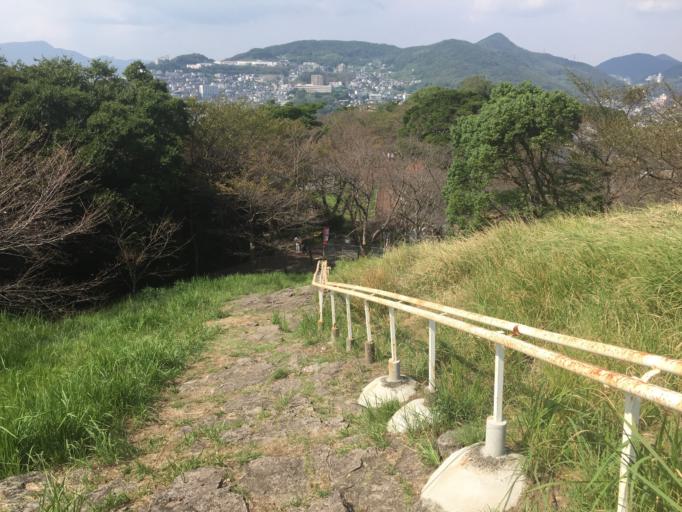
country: JP
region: Nagasaki
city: Nagasaki-shi
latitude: 32.7447
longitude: 129.8865
